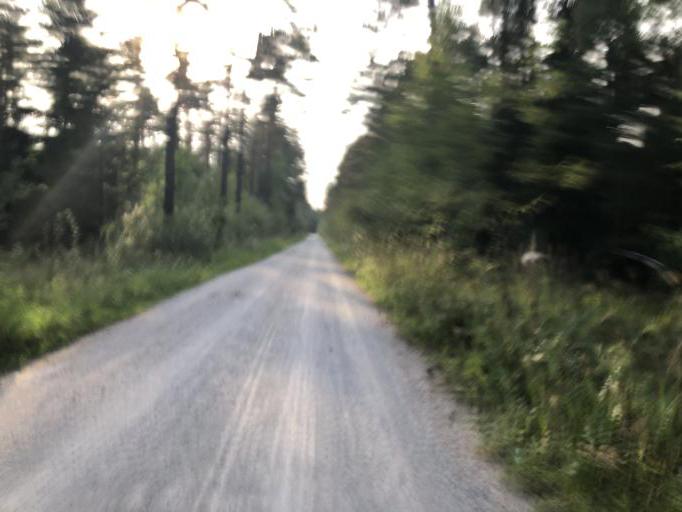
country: DE
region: Bavaria
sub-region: Regierungsbezirk Mittelfranken
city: Buckenhof
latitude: 49.5766
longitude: 11.0509
